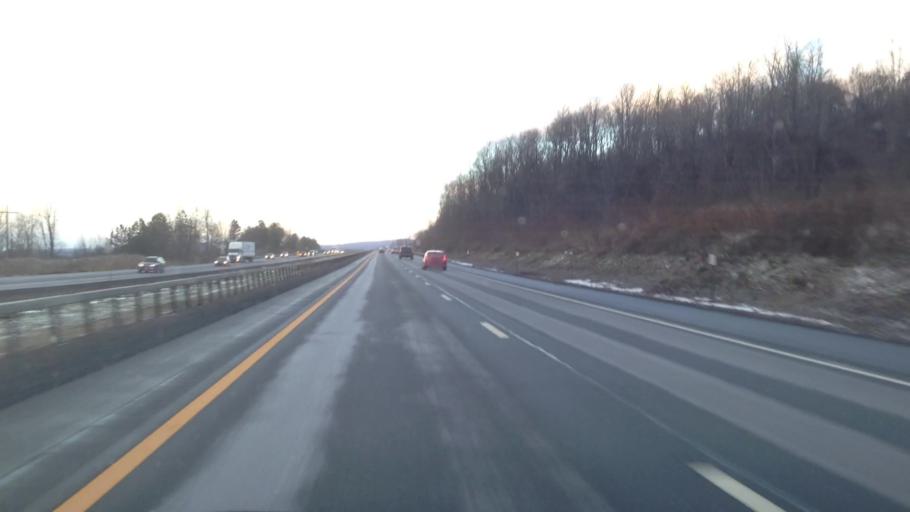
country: US
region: New York
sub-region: Herkimer County
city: Frankfort
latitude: 43.0430
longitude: -75.0545
